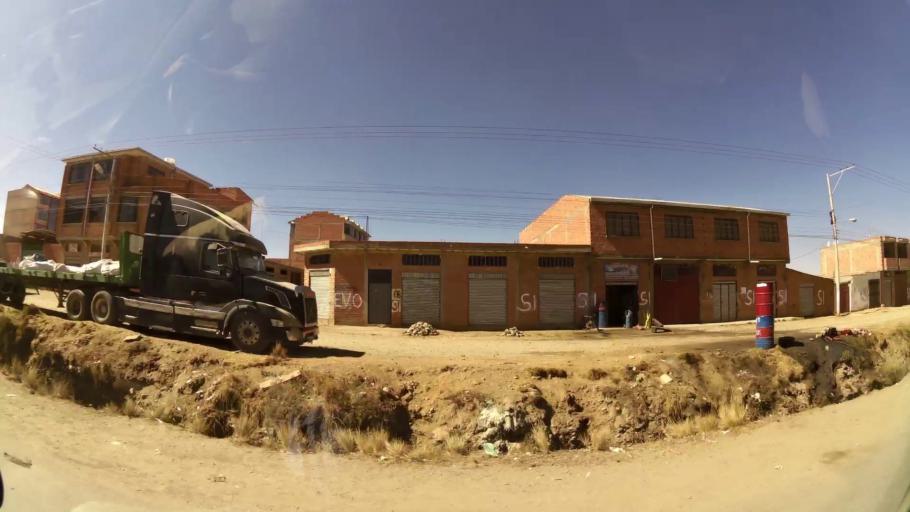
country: BO
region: La Paz
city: La Paz
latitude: -16.5516
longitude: -68.2063
